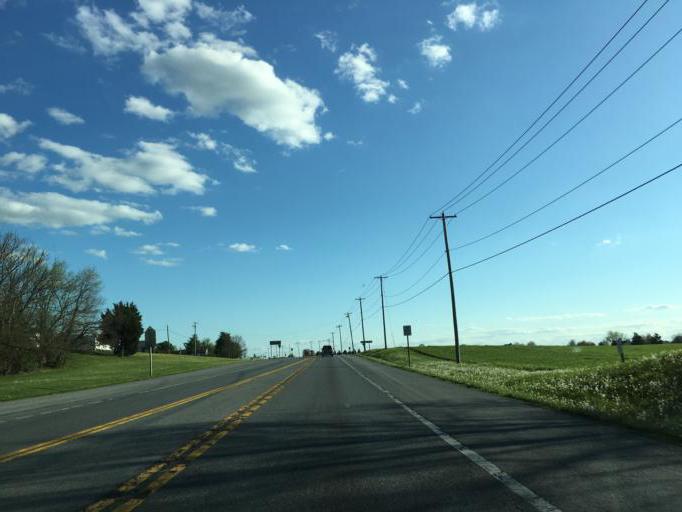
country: US
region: Maryland
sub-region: Frederick County
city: Walkersville
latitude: 39.4712
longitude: -77.3616
